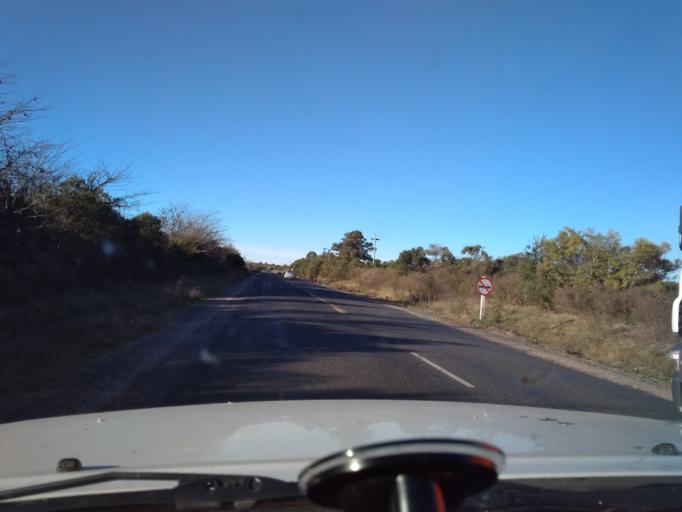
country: UY
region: Canelones
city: San Ramon
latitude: -34.2720
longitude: -55.9448
